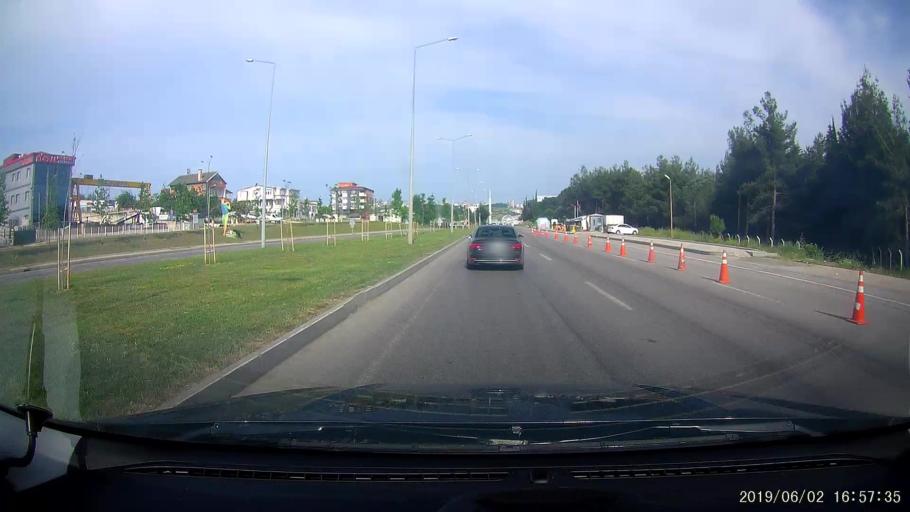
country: TR
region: Samsun
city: Samsun
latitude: 41.2906
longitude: 36.2755
